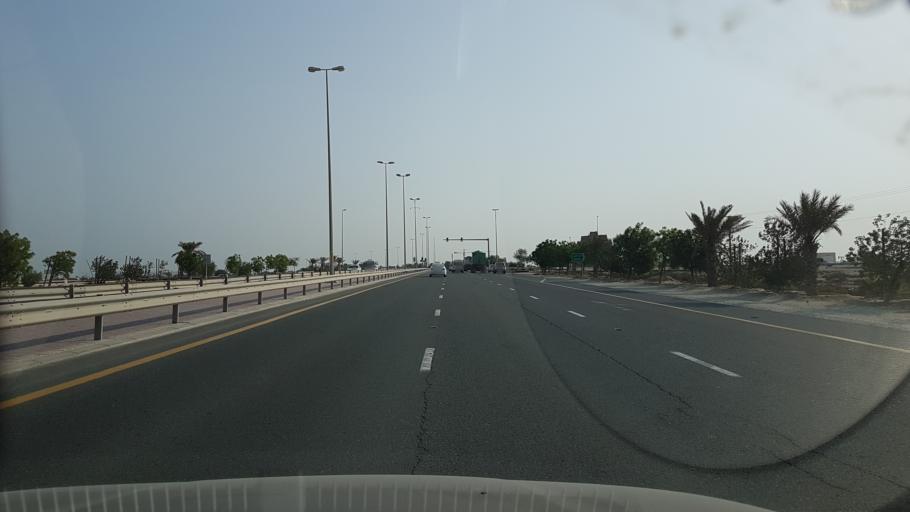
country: BH
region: Central Governorate
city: Dar Kulayb
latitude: 26.0748
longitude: 50.5338
